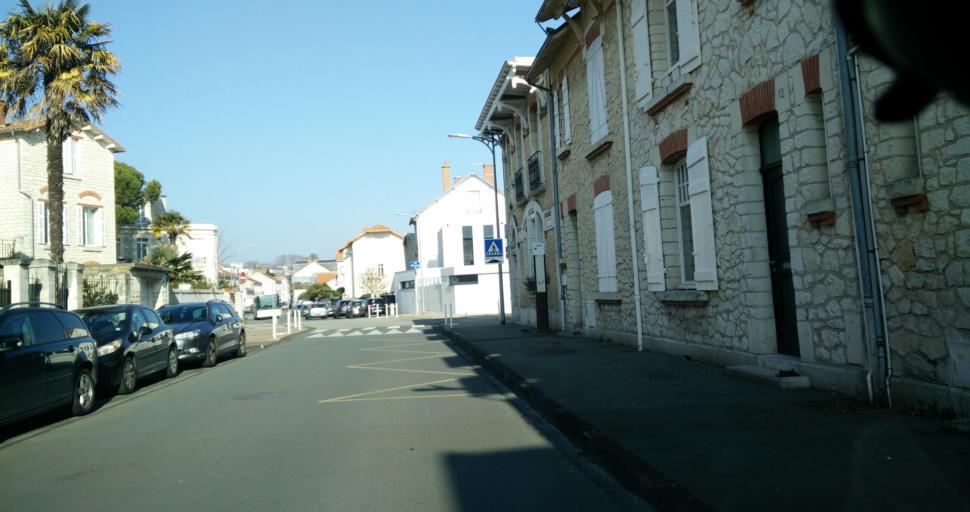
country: FR
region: Poitou-Charentes
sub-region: Departement de la Charente-Maritime
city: La Rochelle
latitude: 46.1636
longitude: -1.1585
